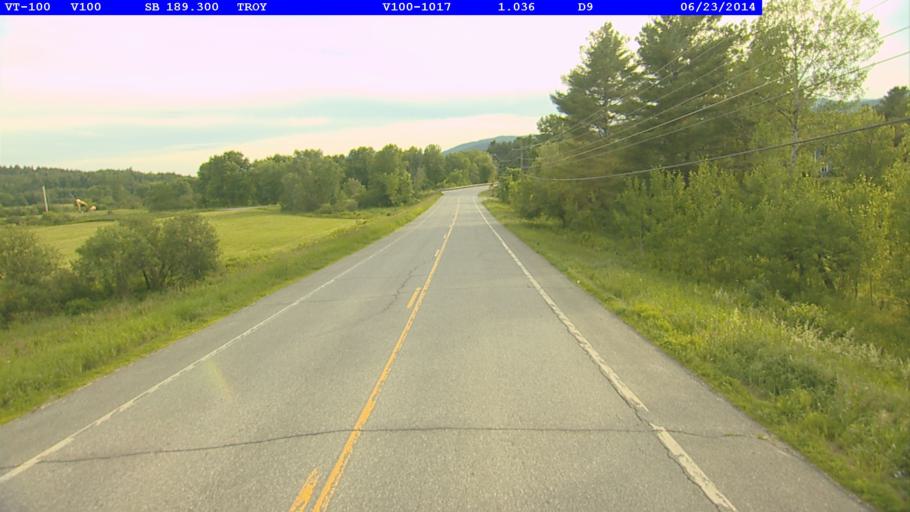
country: US
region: Vermont
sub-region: Orleans County
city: Newport
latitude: 44.9065
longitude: -72.3931
